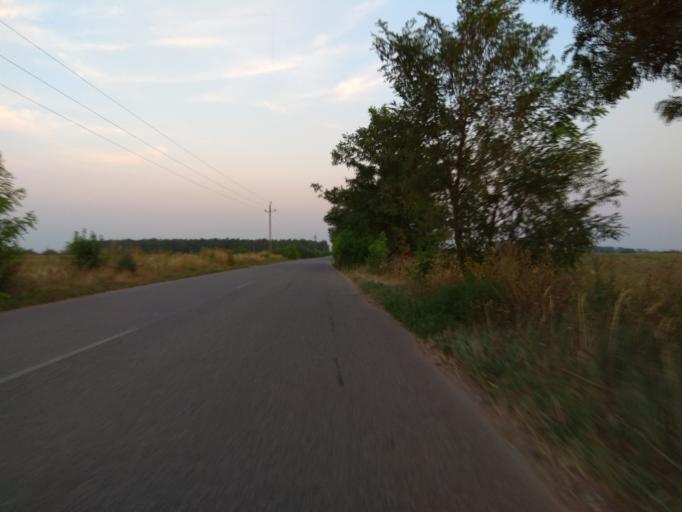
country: HU
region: Borsod-Abauj-Zemplen
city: Emod
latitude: 47.9131
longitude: 20.8500
